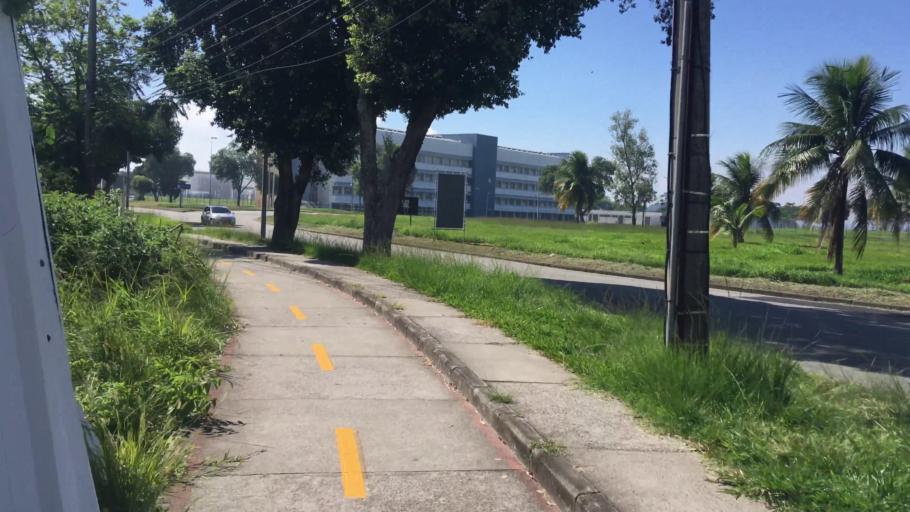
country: BR
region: Rio de Janeiro
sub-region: Rio De Janeiro
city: Rio de Janeiro
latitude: -22.8573
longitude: -43.2305
